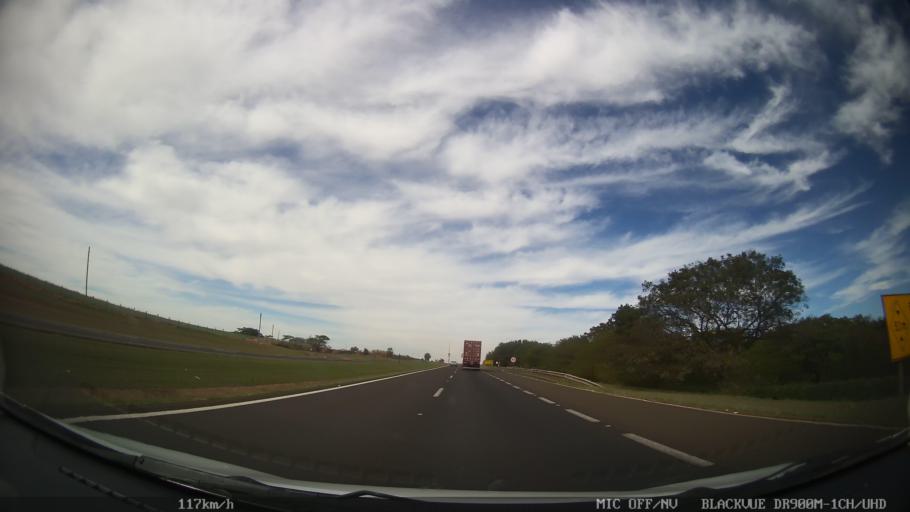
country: BR
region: Sao Paulo
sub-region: Matao
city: Matao
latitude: -21.5570
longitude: -48.4808
